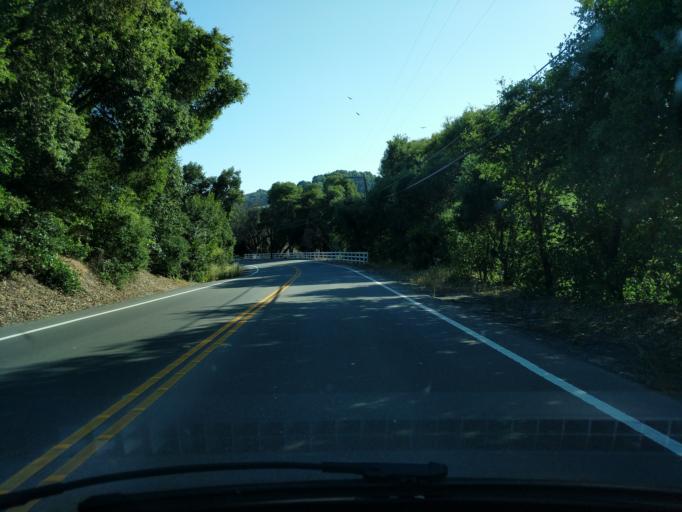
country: US
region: California
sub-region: Contra Costa County
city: San Ramon
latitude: 37.7504
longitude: -122.0307
